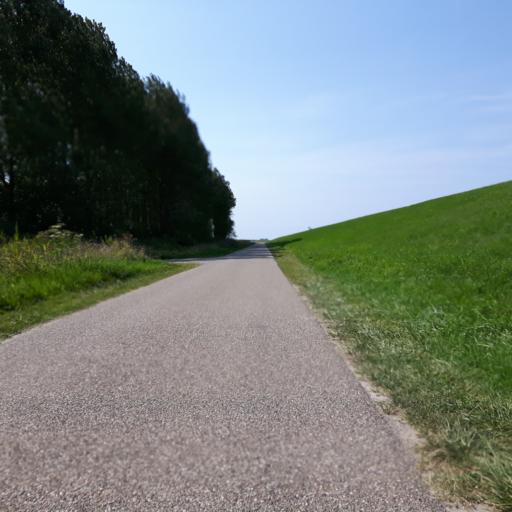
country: NL
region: Zeeland
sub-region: Gemeente Goes
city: Goes
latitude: 51.5408
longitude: 3.8988
